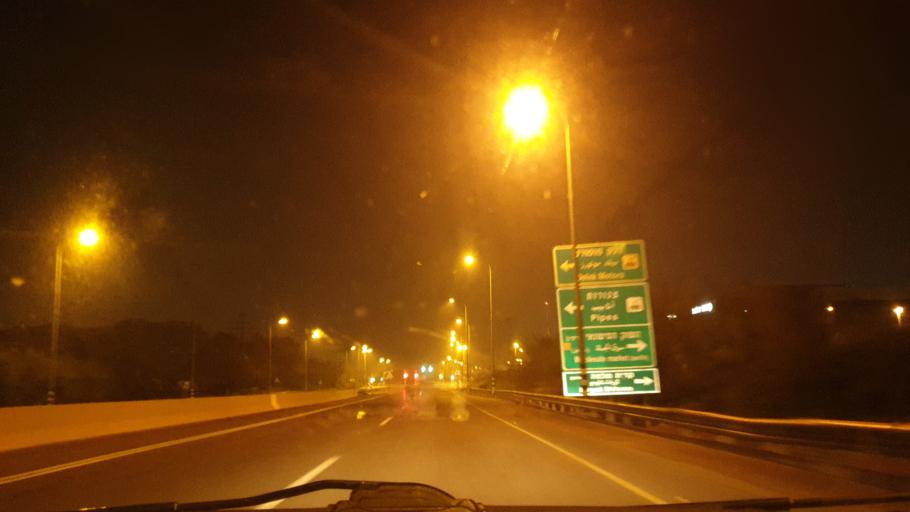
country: IL
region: Central District
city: Kefar Habad
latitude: 31.9619
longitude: 34.8498
